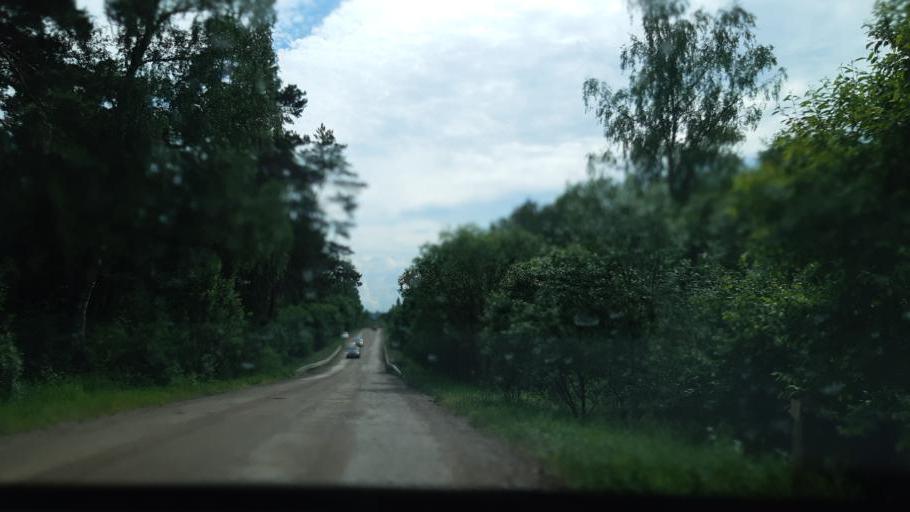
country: RU
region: Moskovskaya
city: Vereya
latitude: 55.2297
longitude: 36.0110
